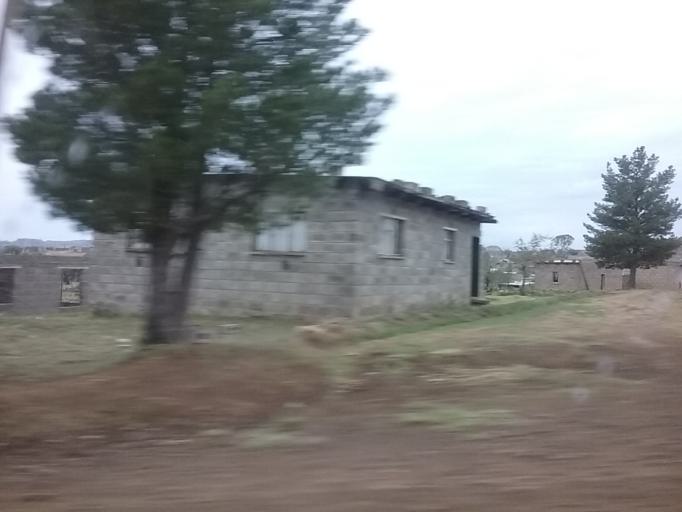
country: LS
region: Berea
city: Teyateyaneng
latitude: -29.1280
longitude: 27.7539
